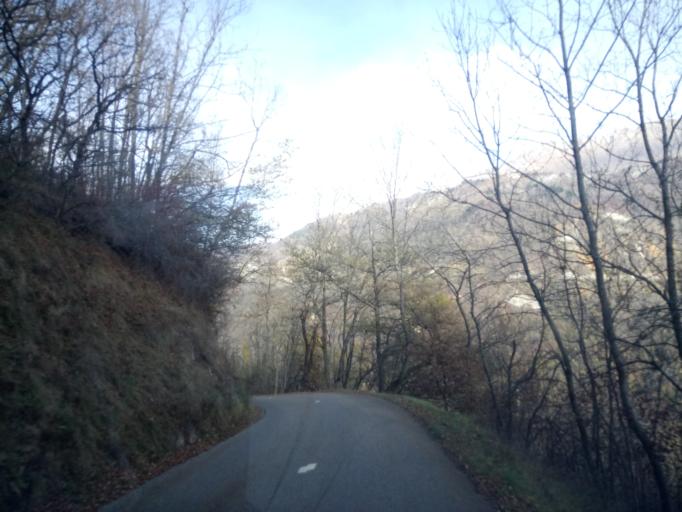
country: FR
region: Rhone-Alpes
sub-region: Departement de la Savoie
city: La Chambre
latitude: 45.3894
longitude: 6.3161
